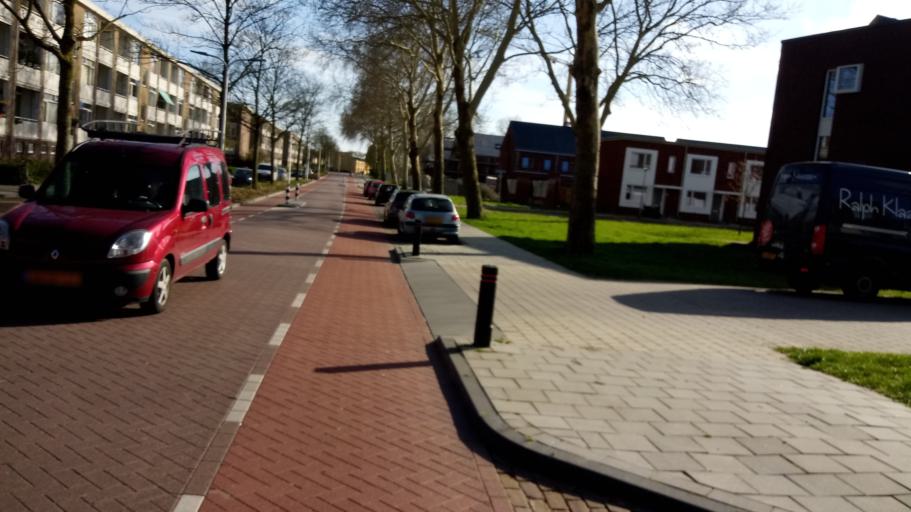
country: NL
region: Gelderland
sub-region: Gemeente Zutphen
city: Zutphen
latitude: 52.1355
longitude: 6.2100
